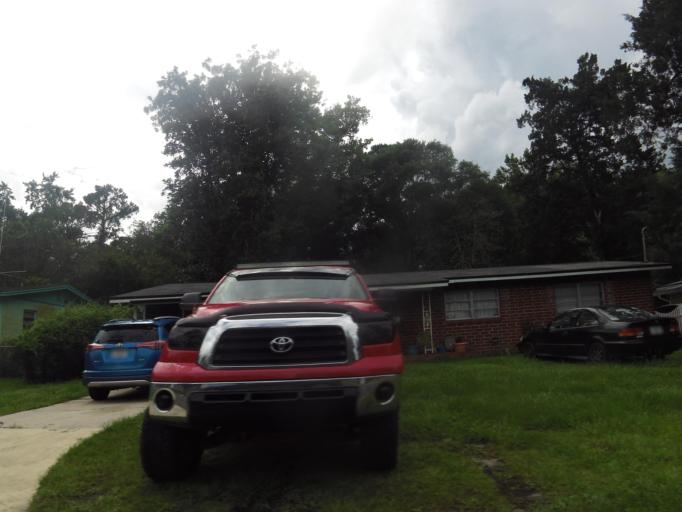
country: US
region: Florida
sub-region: Duval County
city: Jacksonville
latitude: 30.3107
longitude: -81.5373
